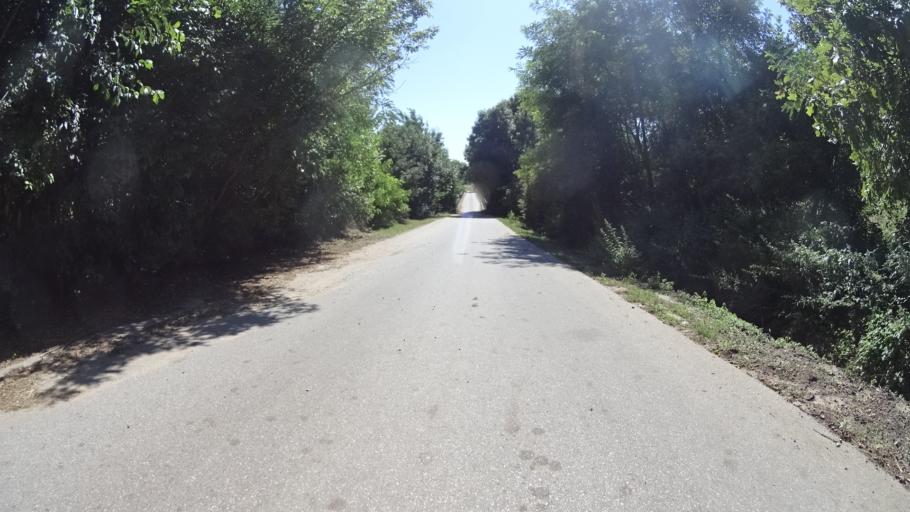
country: PL
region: Masovian Voivodeship
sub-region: Powiat bialobrzeski
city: Bialobrzegi
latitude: 51.6664
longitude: 20.9177
